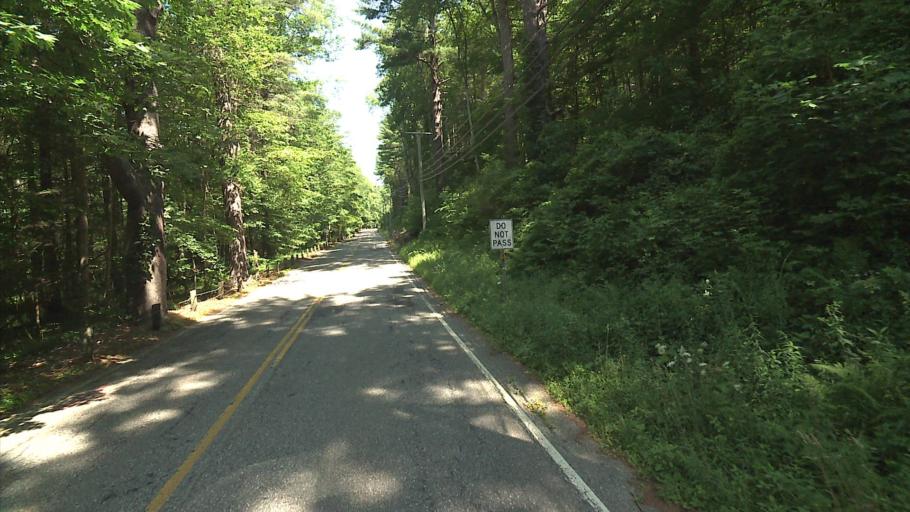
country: US
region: Connecticut
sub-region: Litchfield County
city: Litchfield
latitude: 41.8504
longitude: -73.3286
